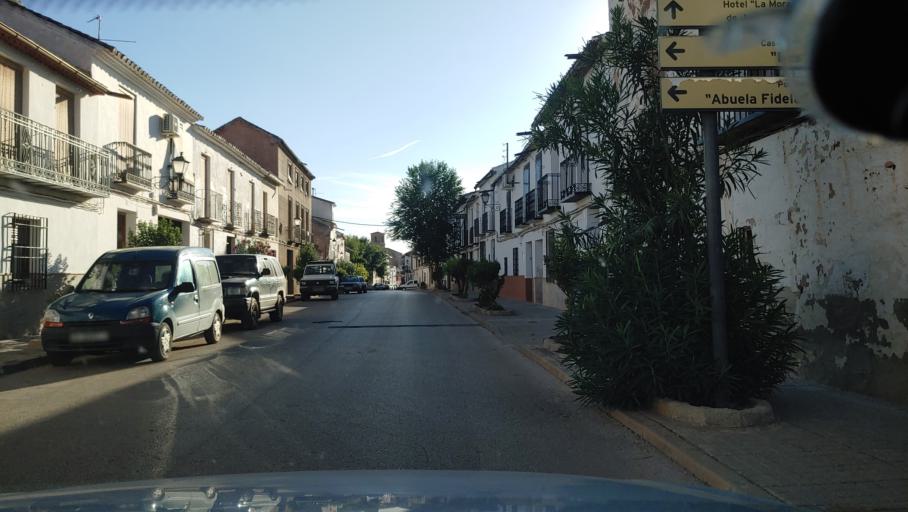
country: ES
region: Castille-La Mancha
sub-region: Provincia de Ciudad Real
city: Infantes
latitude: 38.7395
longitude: -3.0091
